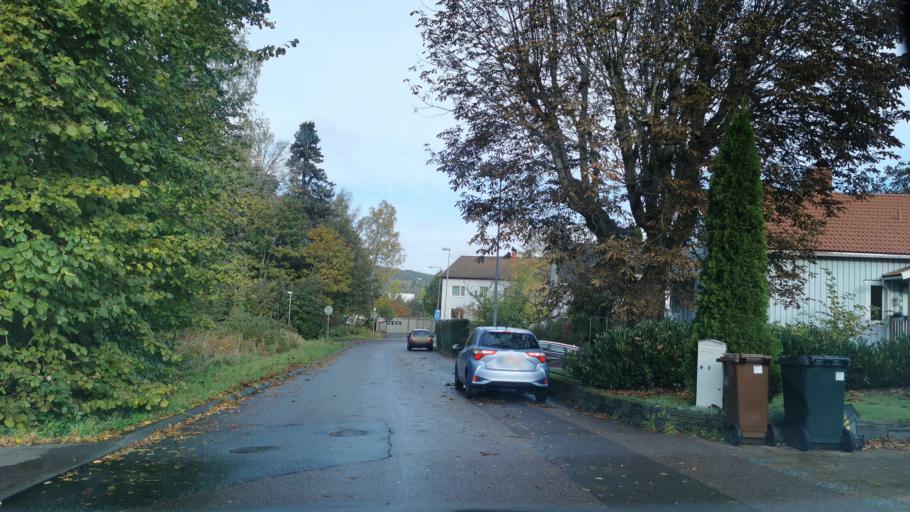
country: SE
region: Vaestra Goetaland
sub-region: Partille Kommun
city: Partille
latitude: 57.7342
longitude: 12.0929
